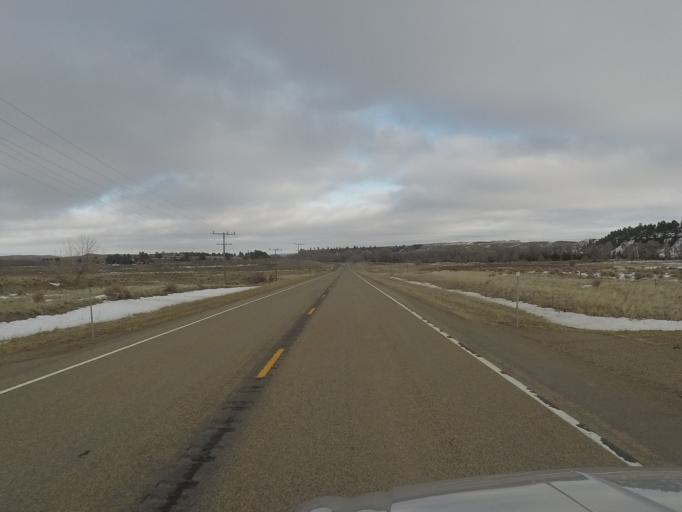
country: US
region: Montana
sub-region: Golden Valley County
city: Ryegate
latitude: 46.2994
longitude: -109.3201
